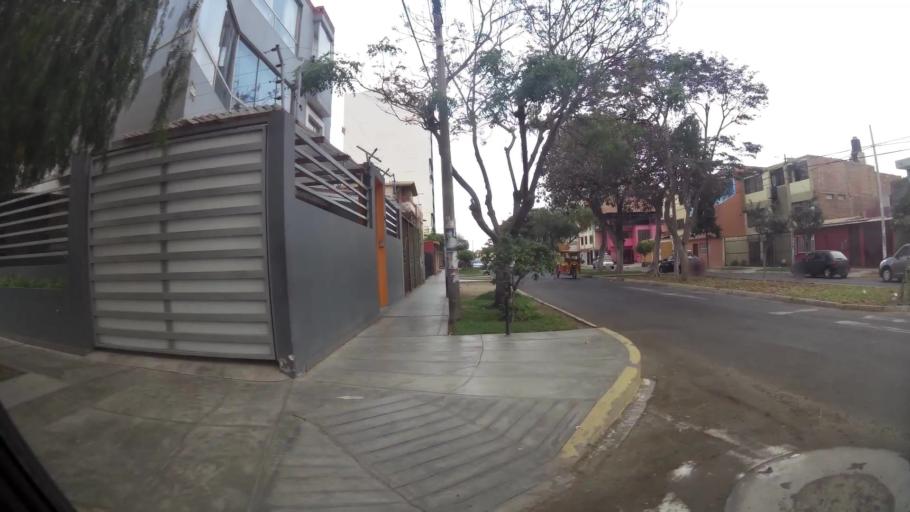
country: PE
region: La Libertad
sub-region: Provincia de Trujillo
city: Trujillo
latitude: -8.1019
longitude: -79.0289
